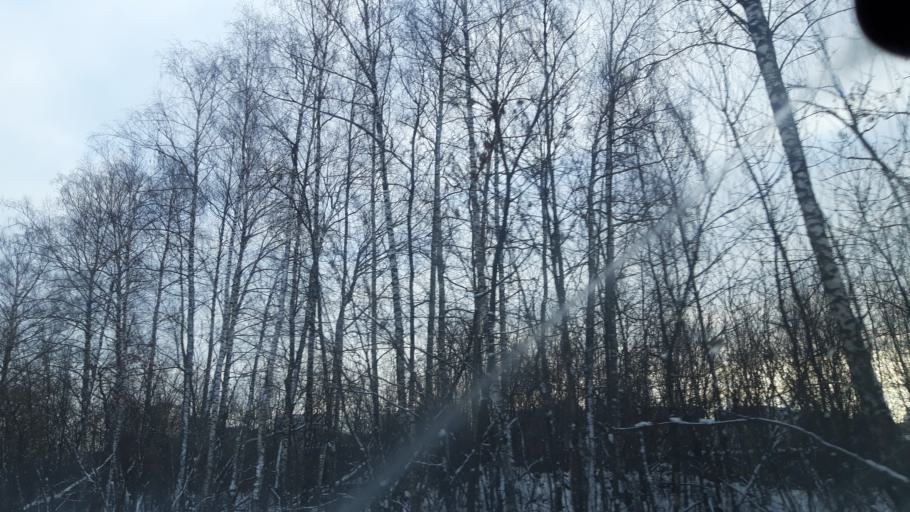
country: RU
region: Moskovskaya
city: Novopodrezkovo
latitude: 55.9098
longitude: 37.3738
